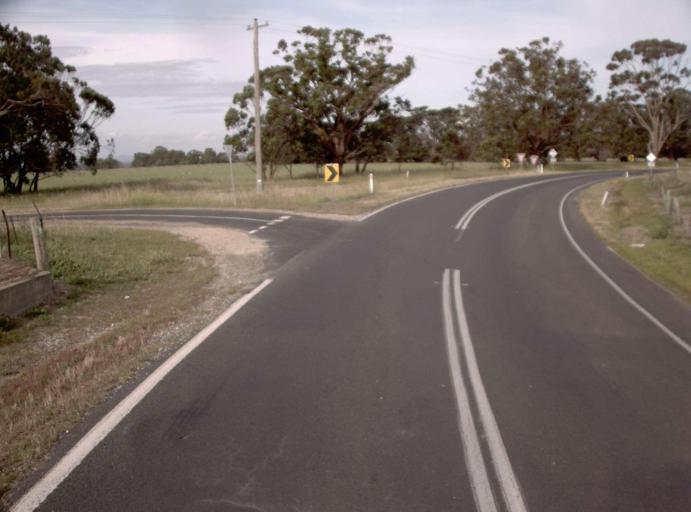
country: AU
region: Victoria
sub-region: Wellington
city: Heyfield
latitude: -38.0123
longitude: 146.6724
